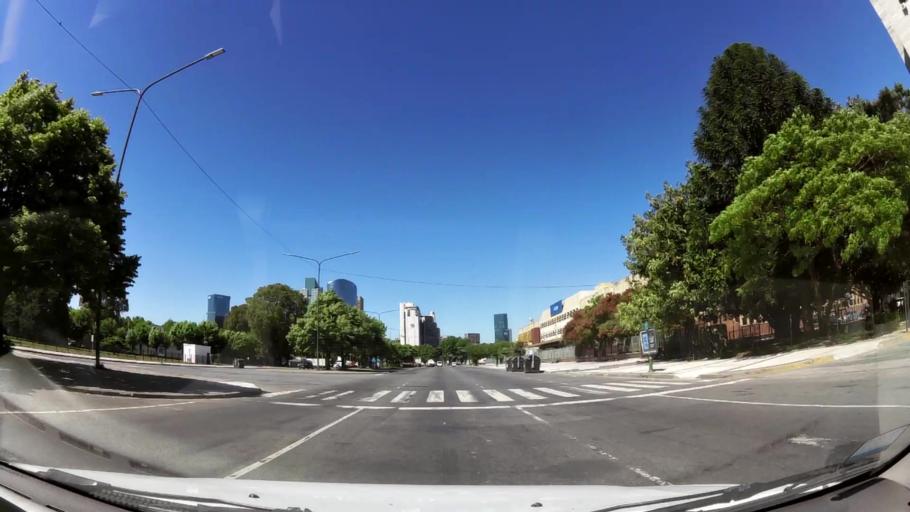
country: AR
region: Buenos Aires F.D.
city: Retiro
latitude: -34.5883
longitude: -58.3690
